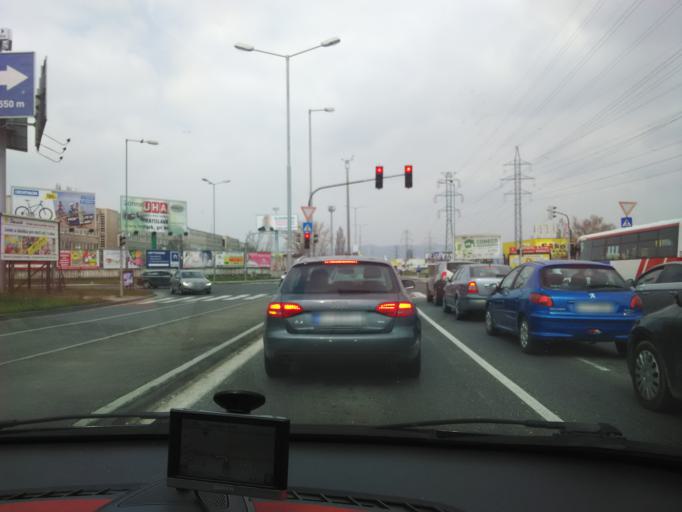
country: SK
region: Bratislavsky
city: Bratislava
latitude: 48.1670
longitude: 17.1778
